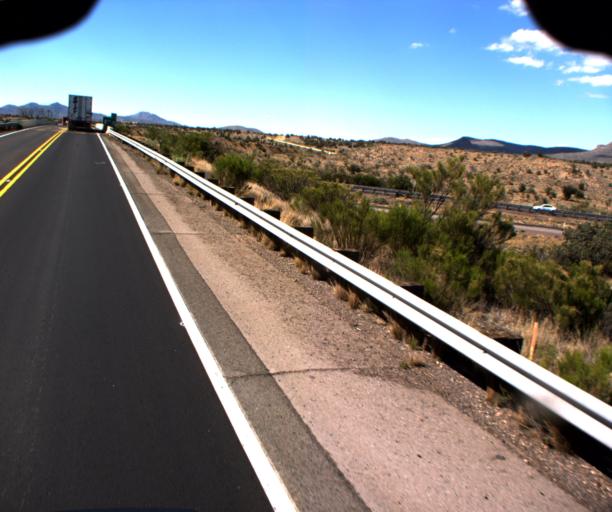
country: US
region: Arizona
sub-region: Mohave County
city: New Kingman-Butler
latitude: 35.1584
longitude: -113.6959
